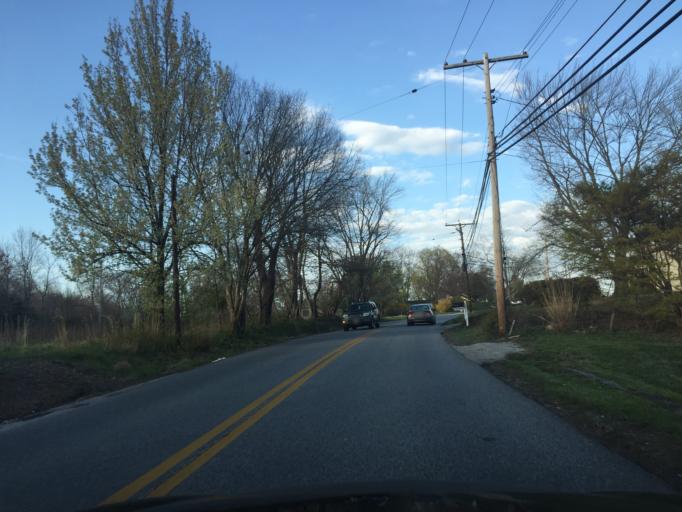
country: US
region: Maryland
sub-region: Baltimore County
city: Perry Hall
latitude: 39.4011
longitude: -76.4520
